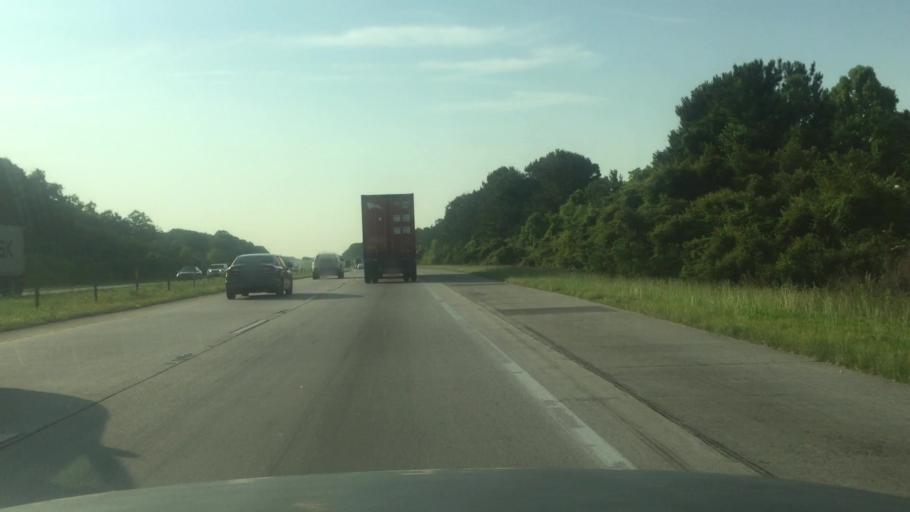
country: US
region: South Carolina
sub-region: Charleston County
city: Mount Pleasant
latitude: 32.8466
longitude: -79.8758
